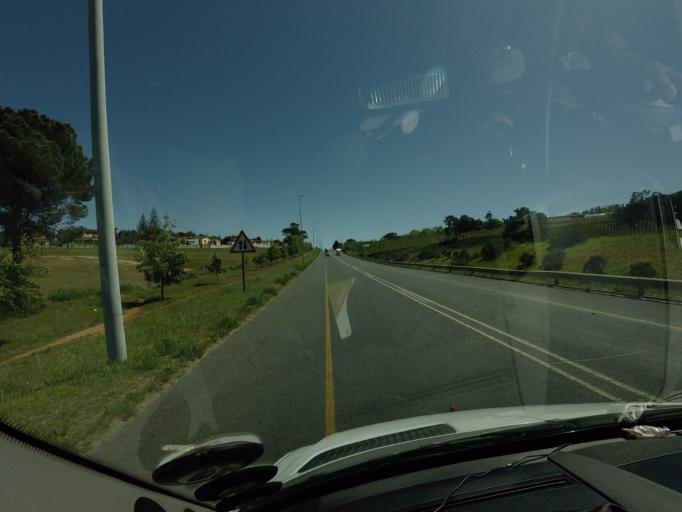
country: ZA
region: Western Cape
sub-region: Cape Winelands District Municipality
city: Stellenbosch
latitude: -33.9064
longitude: 18.8593
